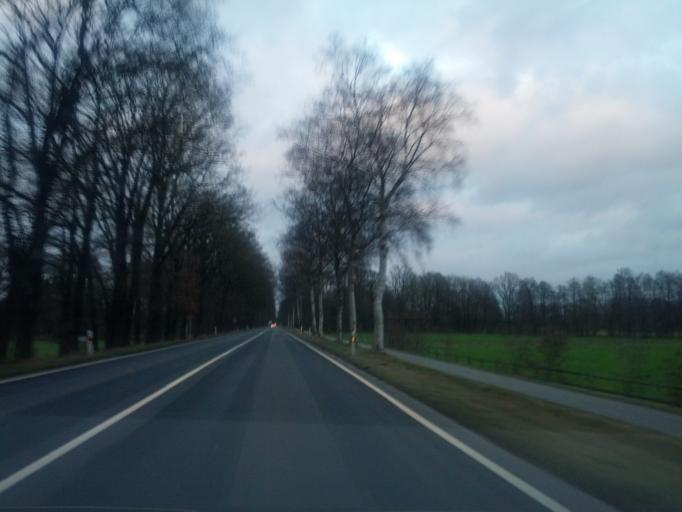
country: DE
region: Lower Saxony
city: Konigsmoor
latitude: 53.2482
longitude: 9.6215
